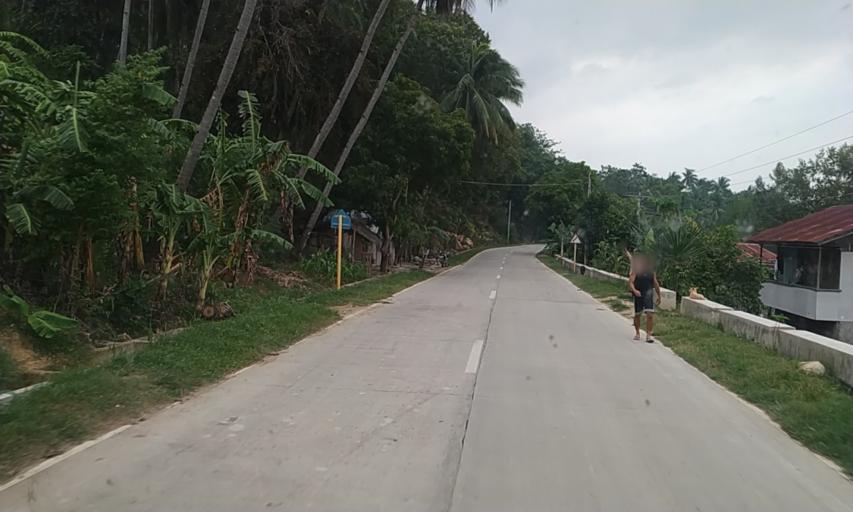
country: PH
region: Central Visayas
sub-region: Province of Negros Oriental
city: Basak
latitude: 10.2133
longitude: 123.3030
